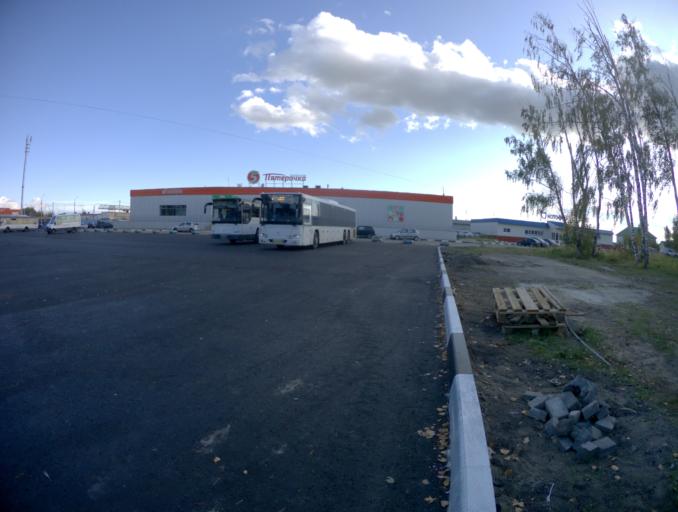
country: RU
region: Moskovskaya
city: Shatura
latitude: 55.5746
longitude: 39.5249
